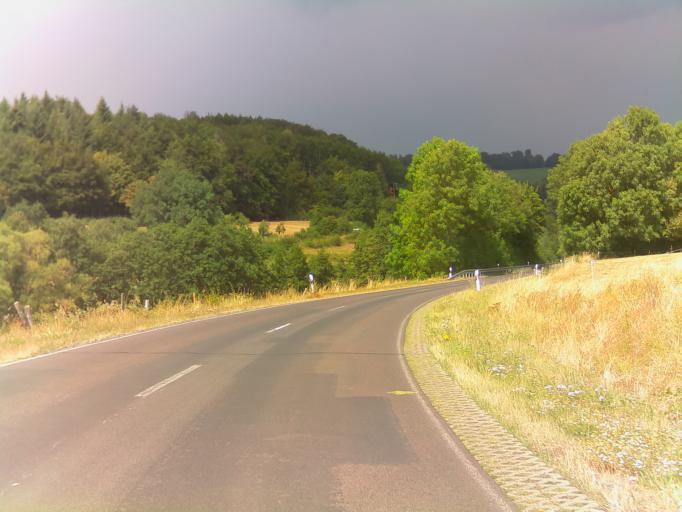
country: DE
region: Hesse
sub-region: Regierungsbezirk Kassel
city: Hosenfeld
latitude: 50.5509
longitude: 9.4317
